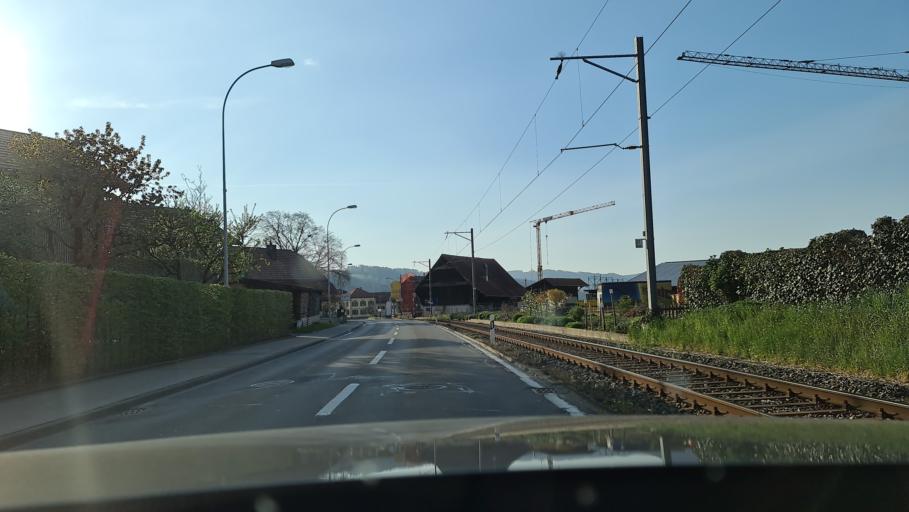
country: CH
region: Lucerne
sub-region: Hochdorf District
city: Hitzkirch
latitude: 47.2263
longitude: 8.2467
